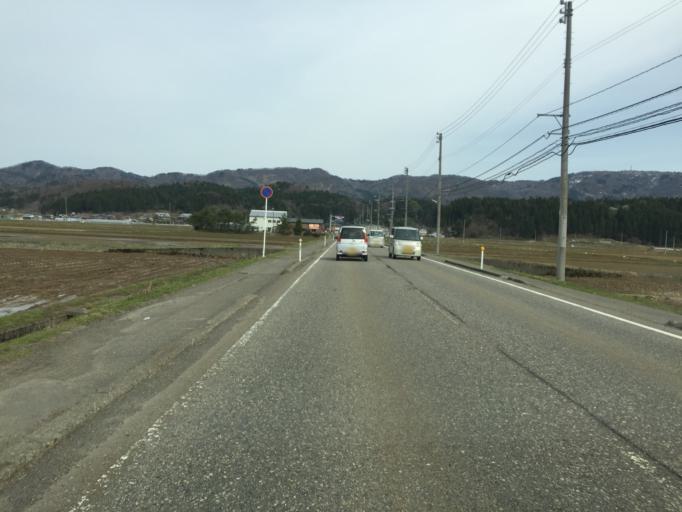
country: JP
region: Niigata
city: Nagaoka
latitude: 37.4543
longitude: 138.8904
